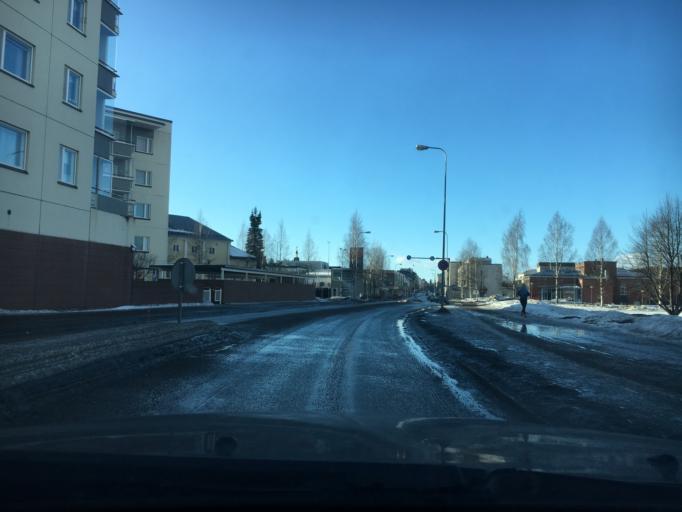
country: FI
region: Kainuu
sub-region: Kajaani
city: Kajaani
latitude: 64.2220
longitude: 27.7397
